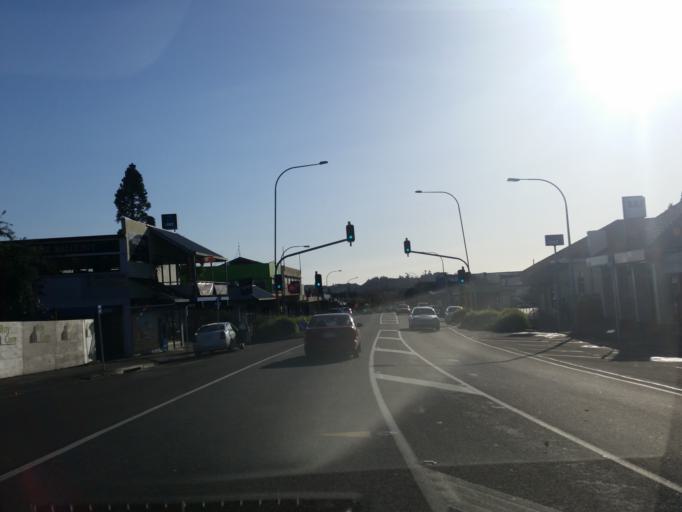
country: NZ
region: Bay of Plenty
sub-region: Western Bay of Plenty District
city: Katikati
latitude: -37.5536
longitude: 175.9172
